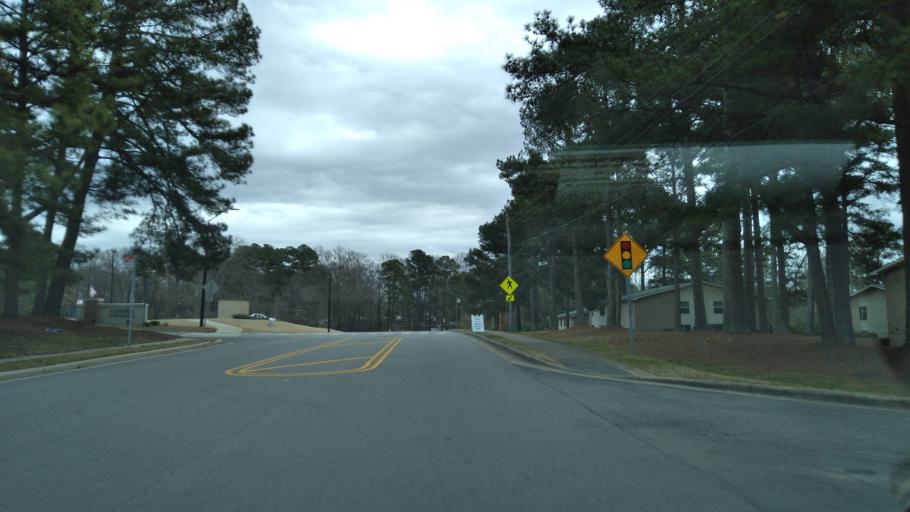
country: US
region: North Carolina
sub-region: Wake County
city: Garner
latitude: 35.7055
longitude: -78.6212
